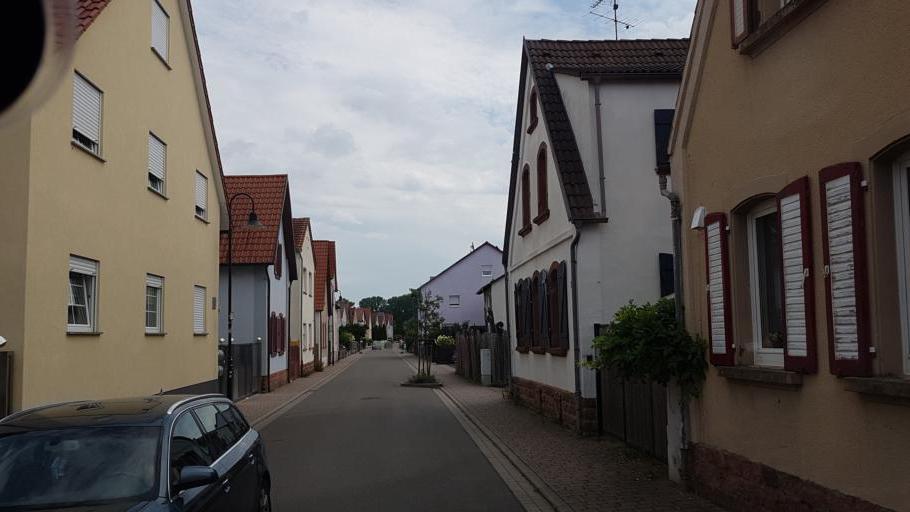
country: DE
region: Rheinland-Pfalz
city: Lingenfeld
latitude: 49.2491
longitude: 8.3451
